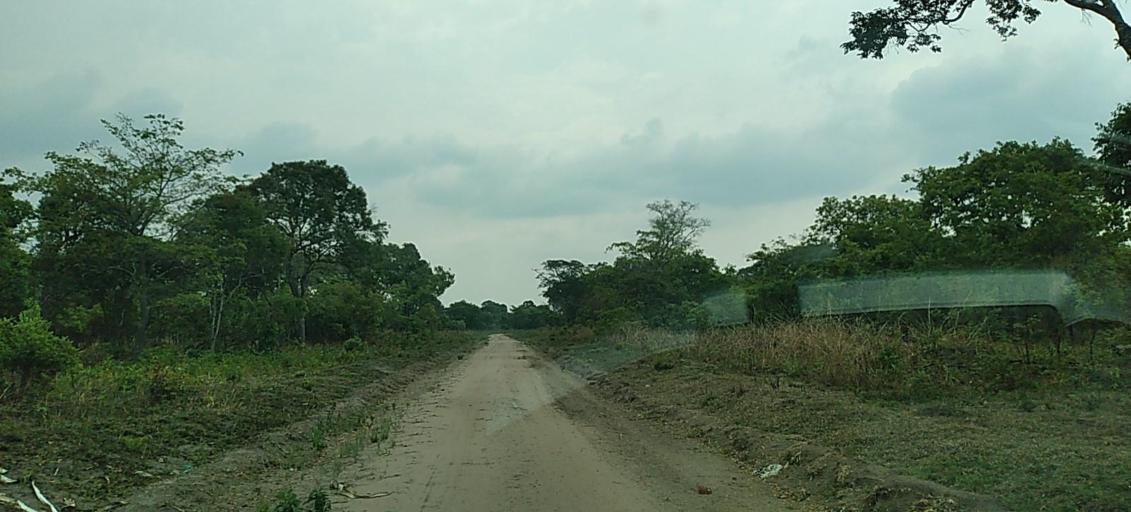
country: ZM
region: North-Western
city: Mwinilunga
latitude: -11.4055
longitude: 24.6298
